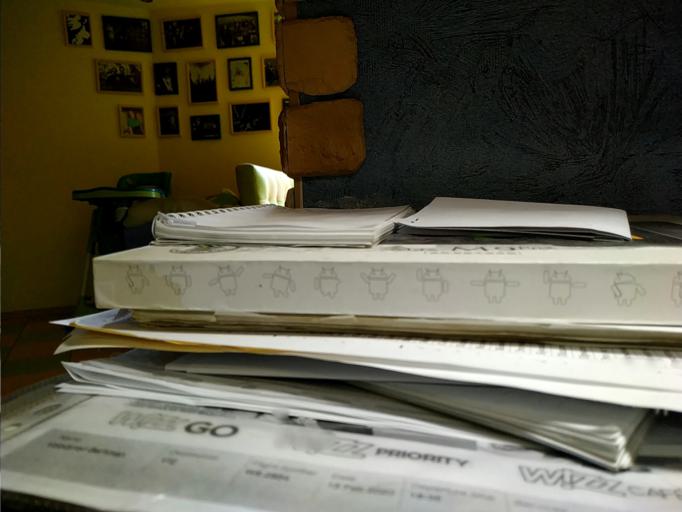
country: RU
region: Pskov
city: Plyussa
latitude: 58.6198
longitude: 29.3872
